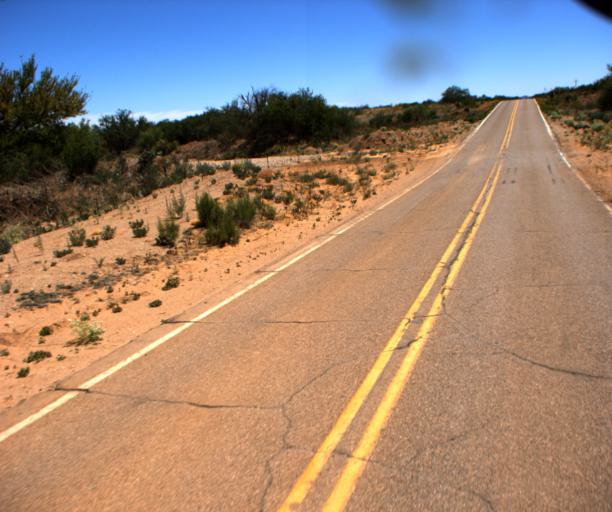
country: US
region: Arizona
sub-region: Pima County
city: Arivaca Junction
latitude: 31.6443
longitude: -111.5001
